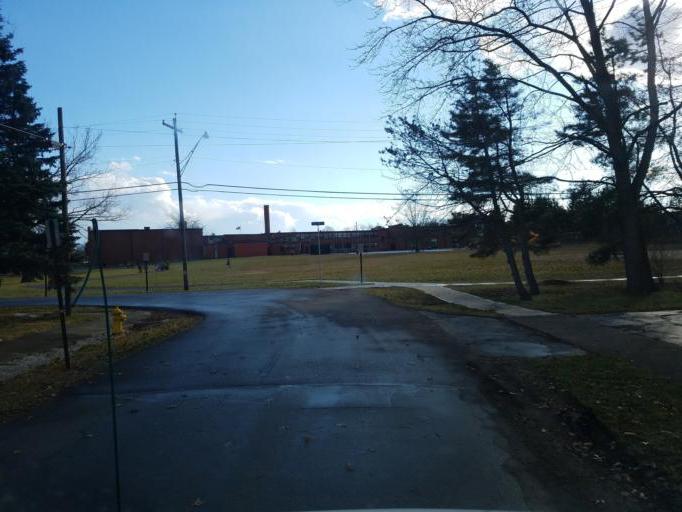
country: US
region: Ohio
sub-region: Delaware County
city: Delaware
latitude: 40.3097
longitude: -83.0931
